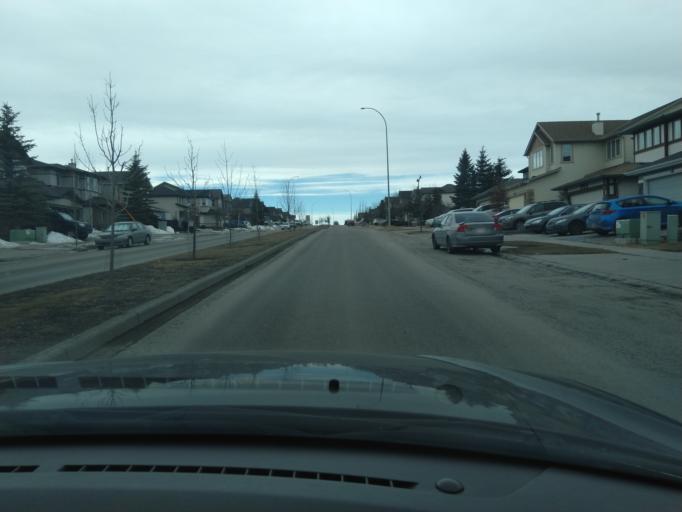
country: CA
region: Alberta
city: Calgary
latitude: 51.1632
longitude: -114.0820
